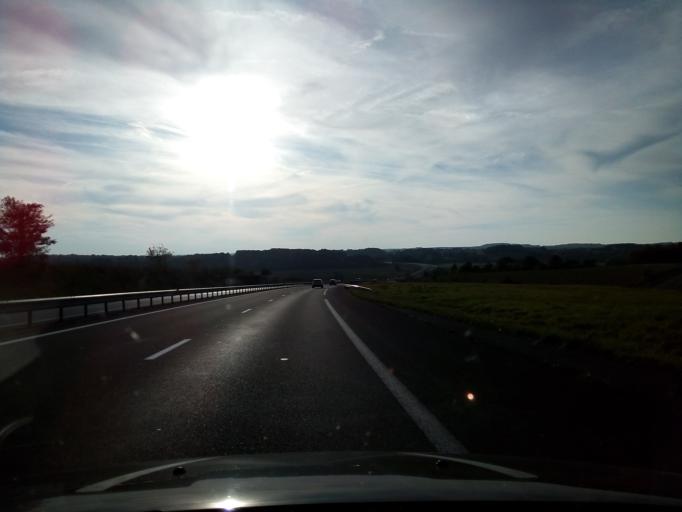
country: FR
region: Poitou-Charentes
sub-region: Departement de la Charente
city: La Rochefoucauld
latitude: 45.7549
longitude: 0.3862
